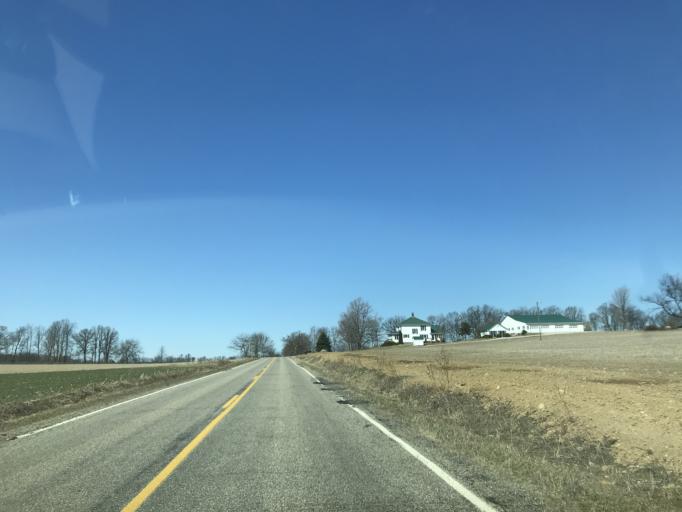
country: US
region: Michigan
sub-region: Hillsdale County
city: Jonesville
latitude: 41.9855
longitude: -84.7251
